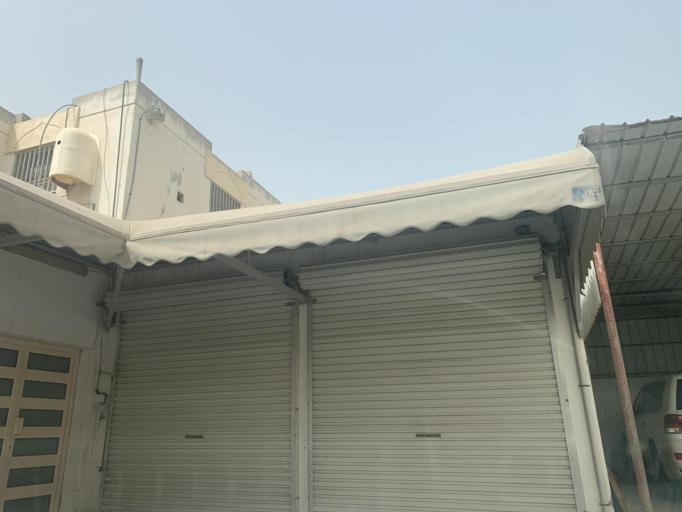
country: BH
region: Northern
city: Madinat `Isa
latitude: 26.1594
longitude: 50.5747
